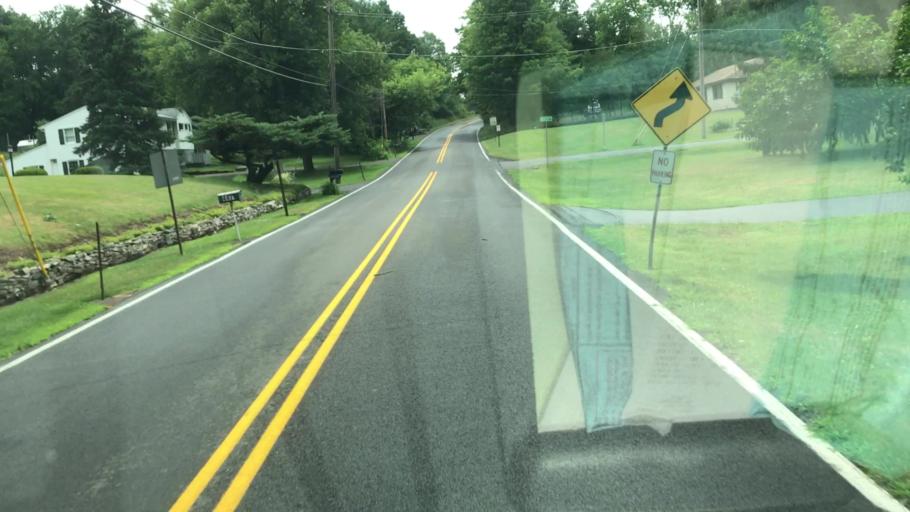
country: US
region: New York
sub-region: Onondaga County
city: Manlius
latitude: 42.9880
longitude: -75.9840
